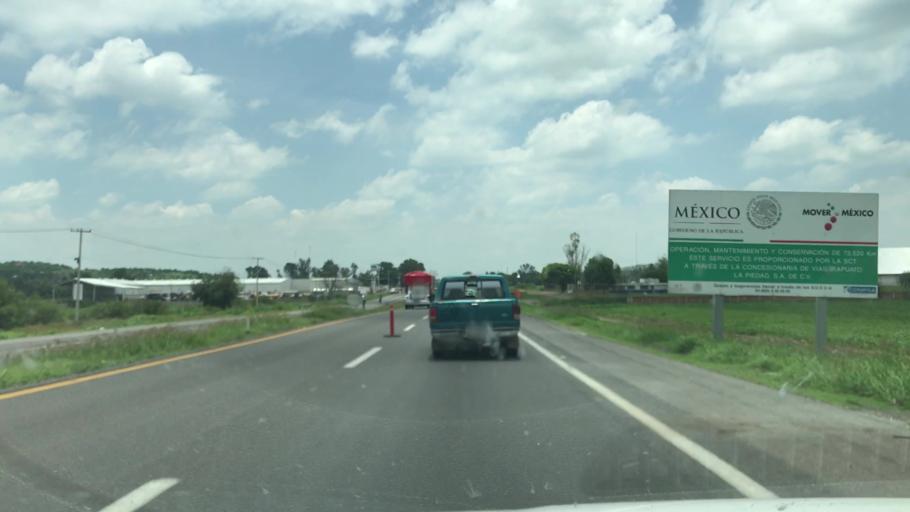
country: MX
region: Guanajuato
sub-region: Irapuato
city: San Ignacio de Rivera (Ojo de Agua)
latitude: 20.5288
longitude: -101.4609
